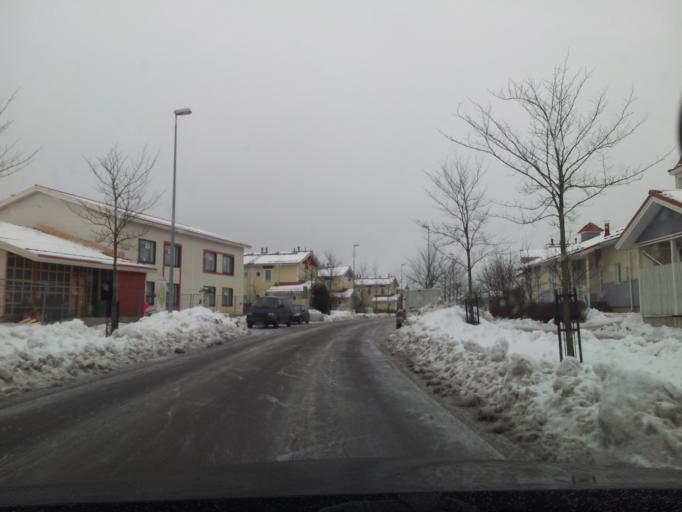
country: FI
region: Uusimaa
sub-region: Helsinki
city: Espoo
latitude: 60.1579
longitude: 24.5515
